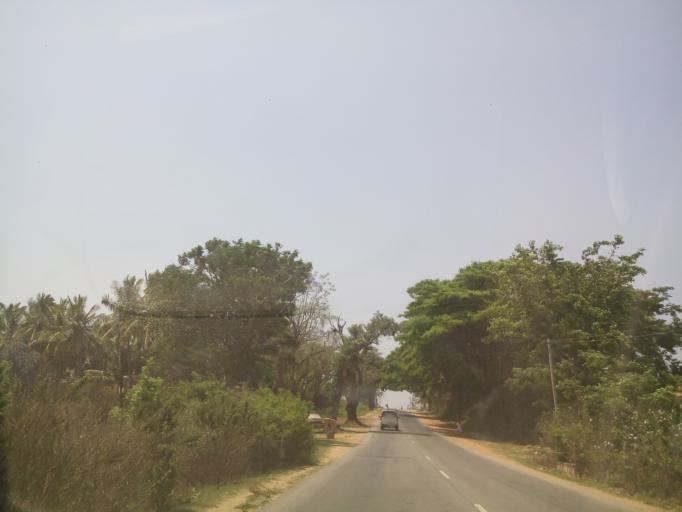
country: IN
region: Karnataka
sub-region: Hassan
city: Hassan
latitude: 12.9904
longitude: 76.0502
